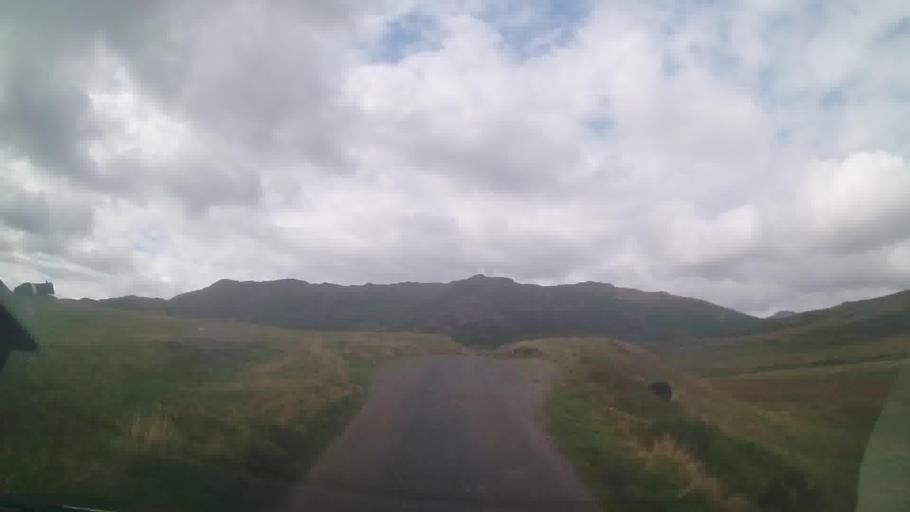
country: GB
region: England
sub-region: Cumbria
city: Keswick
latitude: 54.4054
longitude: -3.1631
